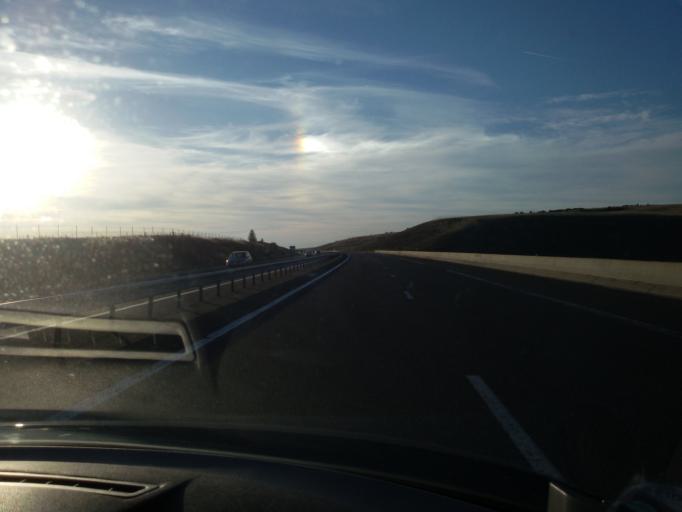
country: FR
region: Midi-Pyrenees
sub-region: Departement de l'Aveyron
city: La Cavalerie
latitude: 44.0242
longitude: 3.1187
